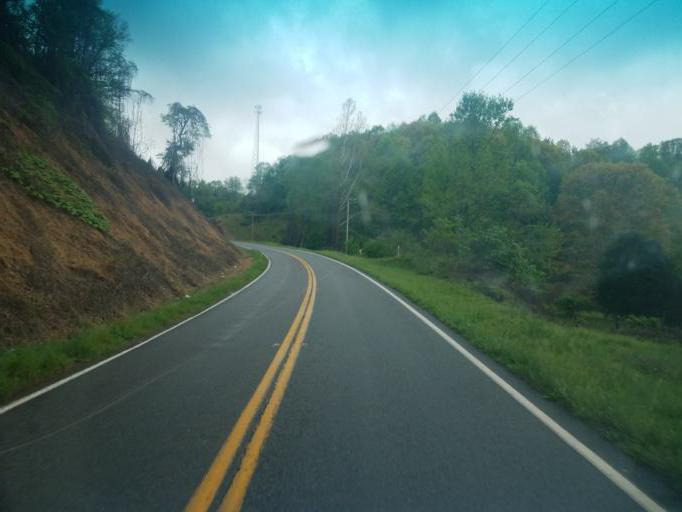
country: US
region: Virginia
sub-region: Washington County
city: Emory
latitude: 36.6429
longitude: -81.7895
